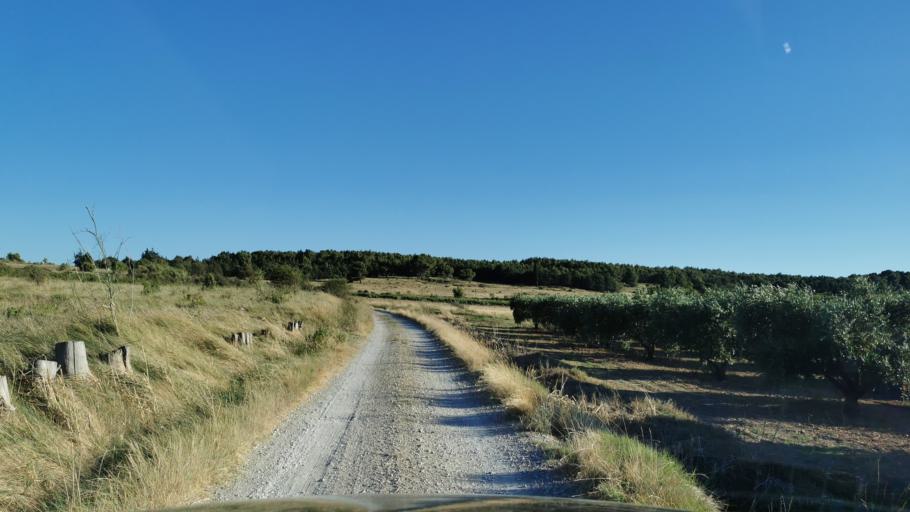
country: FR
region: Languedoc-Roussillon
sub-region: Departement de l'Aude
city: Ouveillan
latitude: 43.2737
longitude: 2.9769
